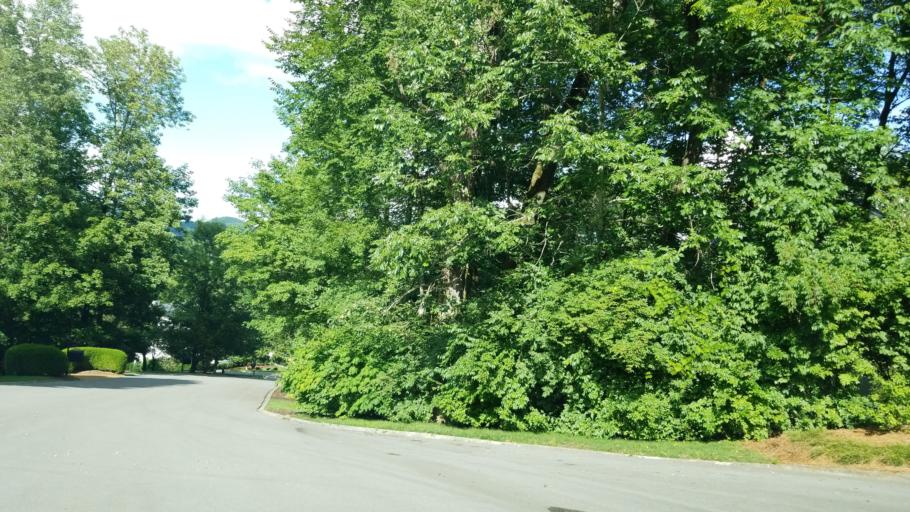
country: US
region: Tennessee
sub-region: Davidson County
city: Forest Hills
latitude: 36.0290
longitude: -86.8422
